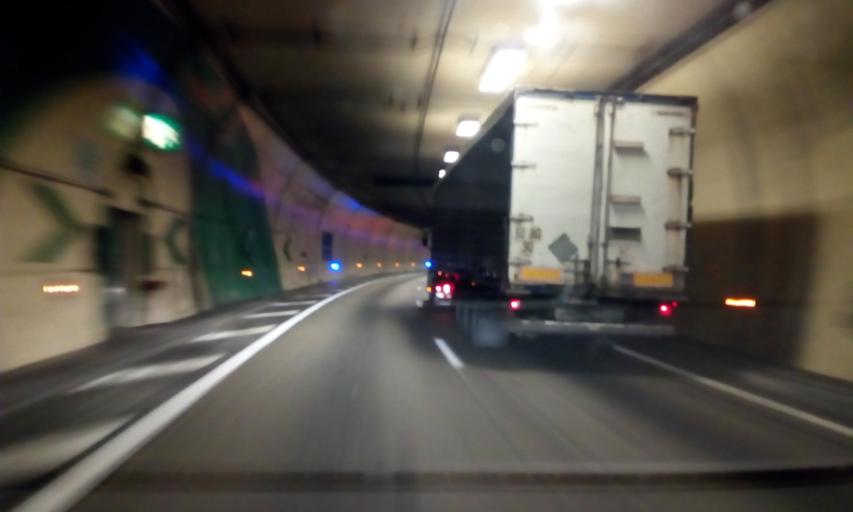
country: FR
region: Provence-Alpes-Cote d'Azur
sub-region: Departement du Var
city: Toulon
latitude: 43.1237
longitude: 5.9336
